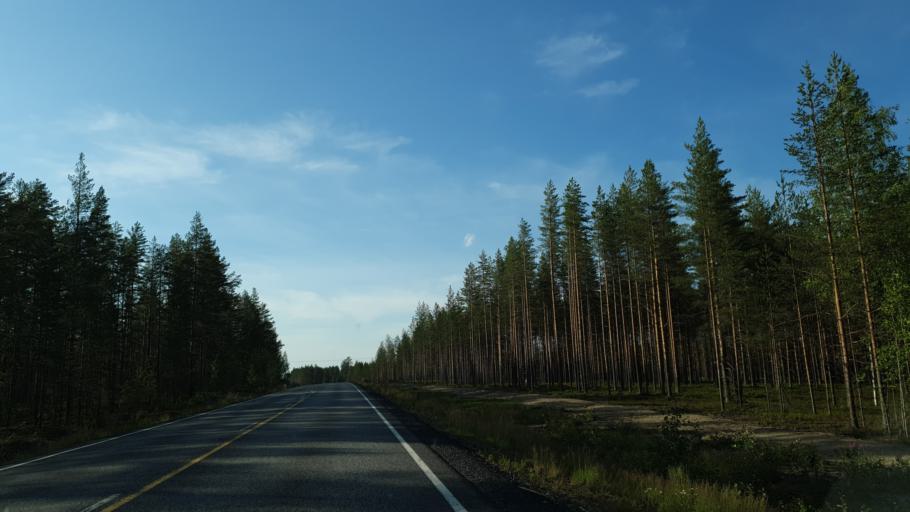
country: FI
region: Kainuu
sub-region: Kehys-Kainuu
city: Kuhmo
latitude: 64.0897
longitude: 29.4815
